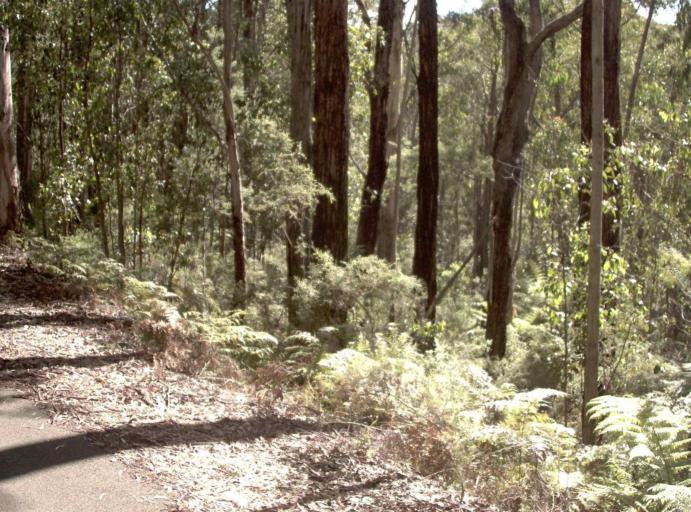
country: AU
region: Victoria
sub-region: East Gippsland
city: Lakes Entrance
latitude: -37.4133
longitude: 148.1197
